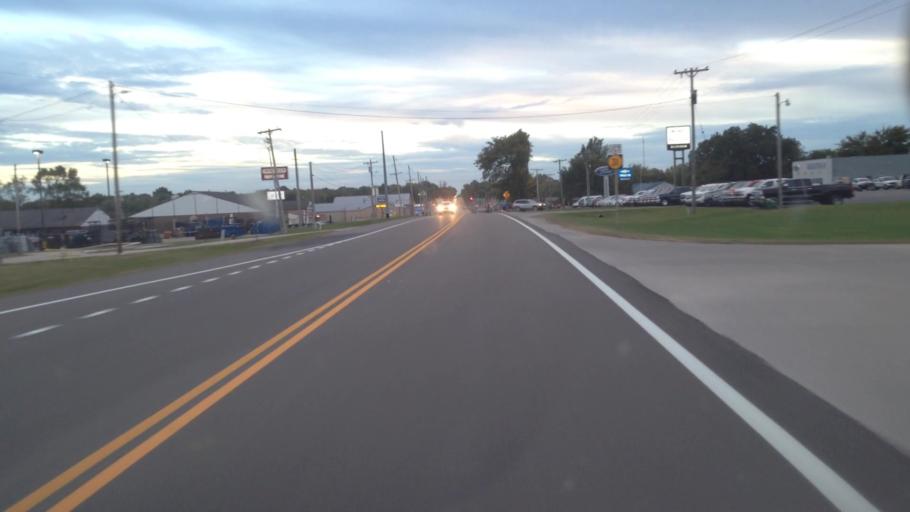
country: US
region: Kansas
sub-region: Anderson County
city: Garnett
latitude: 38.2915
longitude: -95.2493
